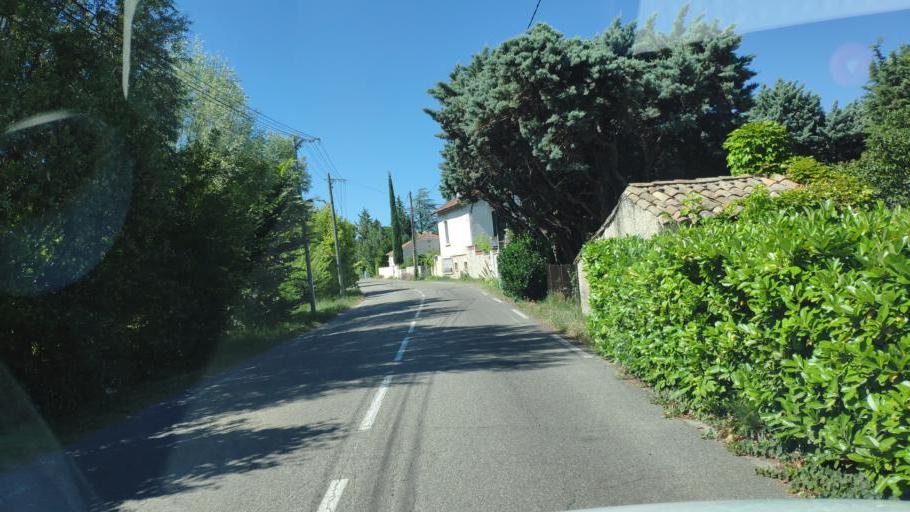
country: FR
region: Provence-Alpes-Cote d'Azur
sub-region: Departement du Vaucluse
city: Chateauneuf-de-Gadagne
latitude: 43.9282
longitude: 4.9507
